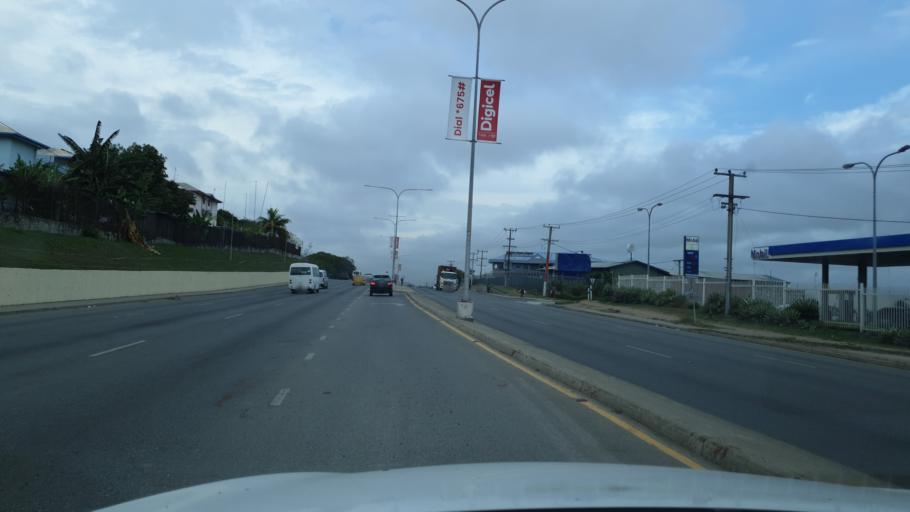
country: PG
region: National Capital
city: Port Moresby
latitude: -9.4373
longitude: 147.1799
